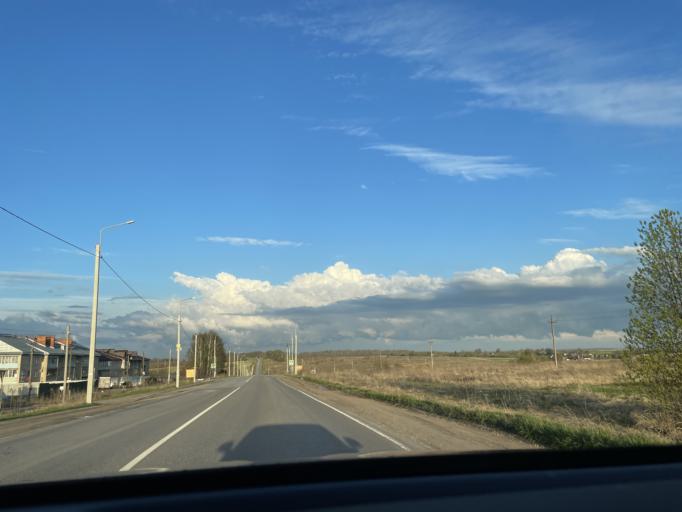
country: RU
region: Tula
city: Novogurovskiy
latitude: 54.5255
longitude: 37.4138
